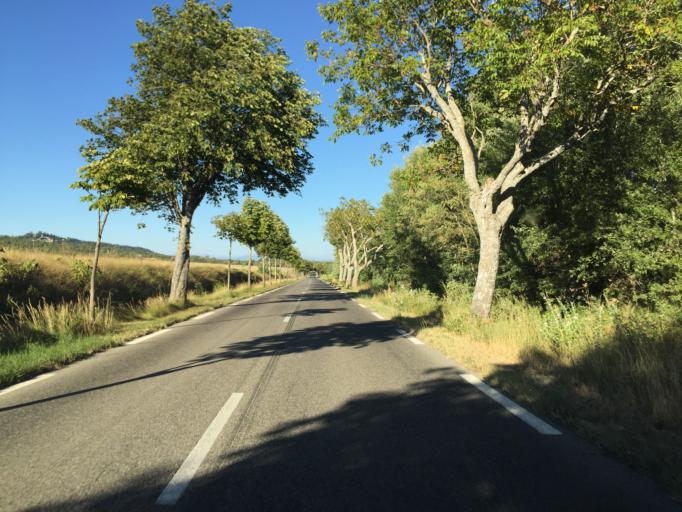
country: FR
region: Provence-Alpes-Cote d'Azur
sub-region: Departement des Alpes-de-Haute-Provence
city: Reillanne
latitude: 43.8686
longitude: 5.6903
